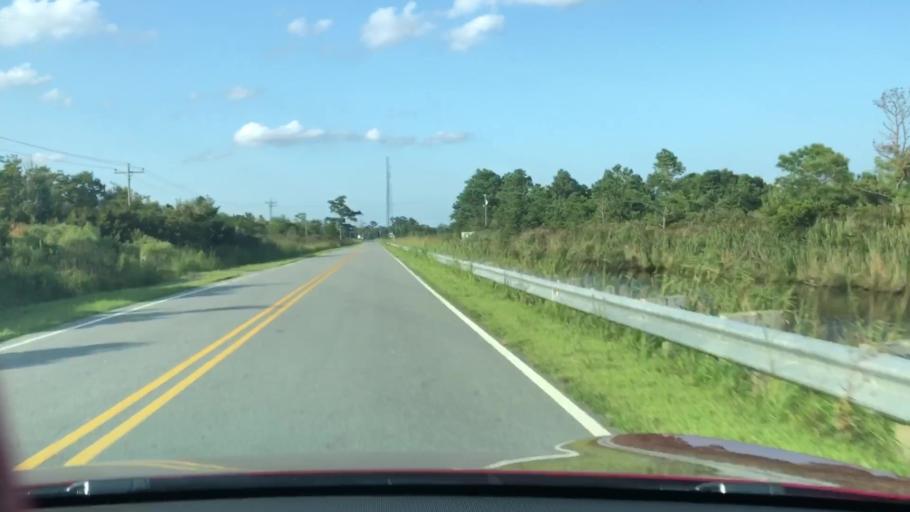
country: US
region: North Carolina
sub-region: Dare County
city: Wanchese
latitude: 35.6992
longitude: -75.7722
